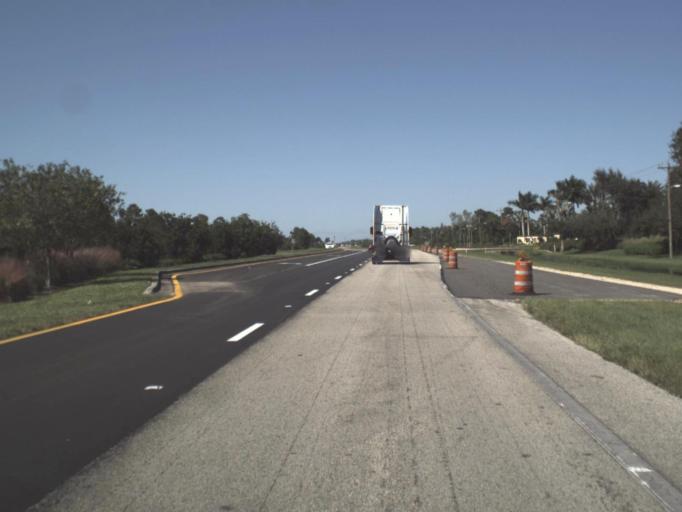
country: US
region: Florida
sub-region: Lee County
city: Suncoast Estates
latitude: 26.7652
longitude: -81.9284
